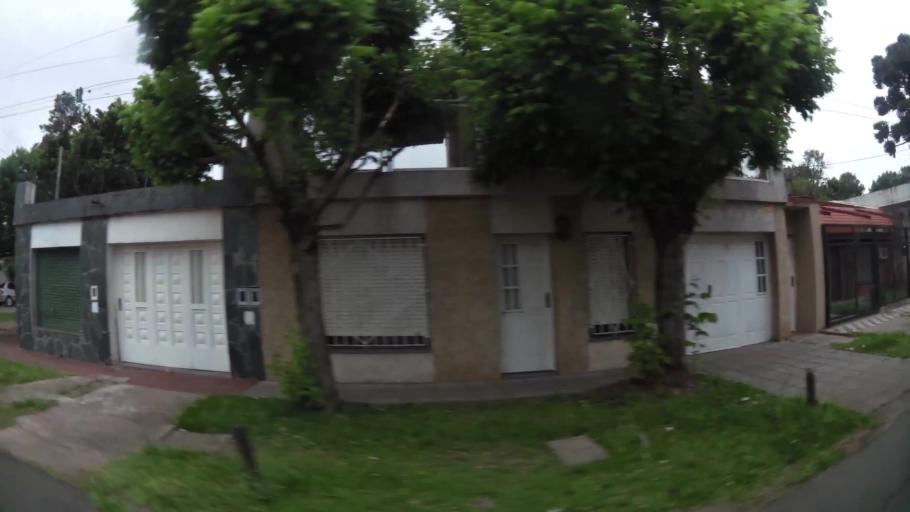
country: AR
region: Santa Fe
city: Granadero Baigorria
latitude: -32.8941
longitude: -60.6997
